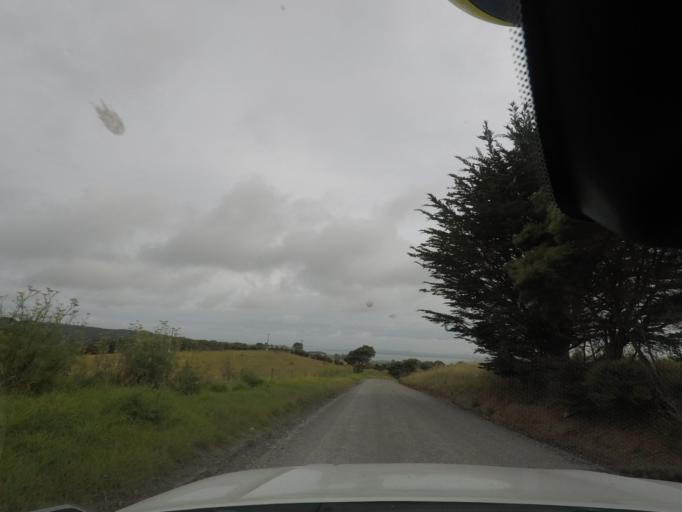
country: NZ
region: Auckland
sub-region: Auckland
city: Parakai
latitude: -36.4820
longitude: 174.2539
